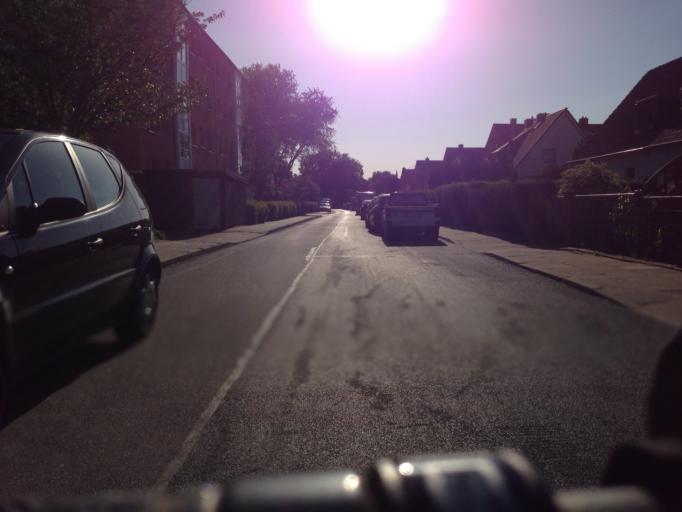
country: DE
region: Schleswig-Holstein
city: Barsbuettel
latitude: 53.5720
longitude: 10.1674
